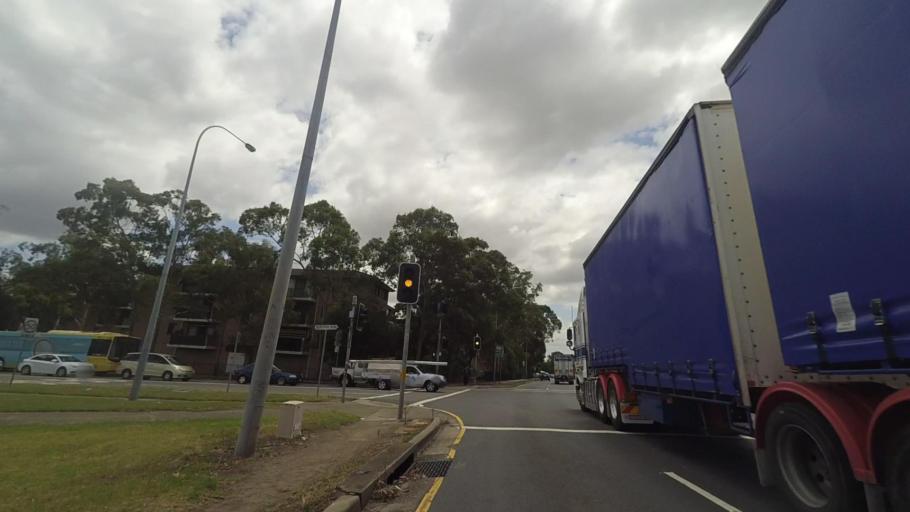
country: AU
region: New South Wales
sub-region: Fairfield
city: Cabramatta West
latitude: -33.9244
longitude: 150.9181
